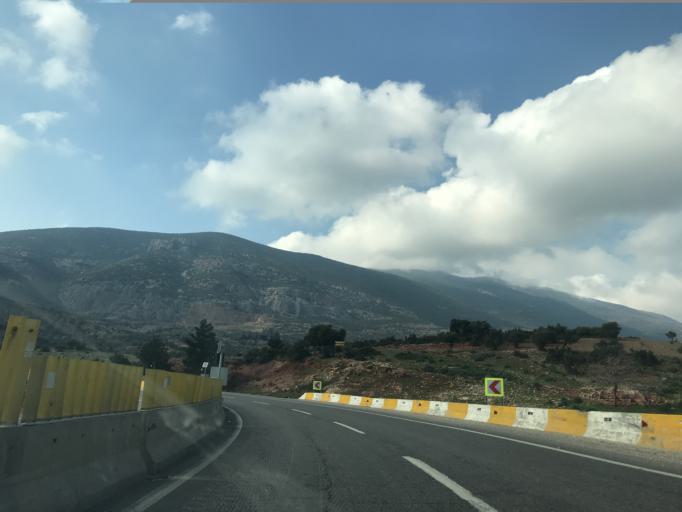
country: TR
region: Hatay
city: Kirikhan
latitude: 36.4865
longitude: 36.2795
